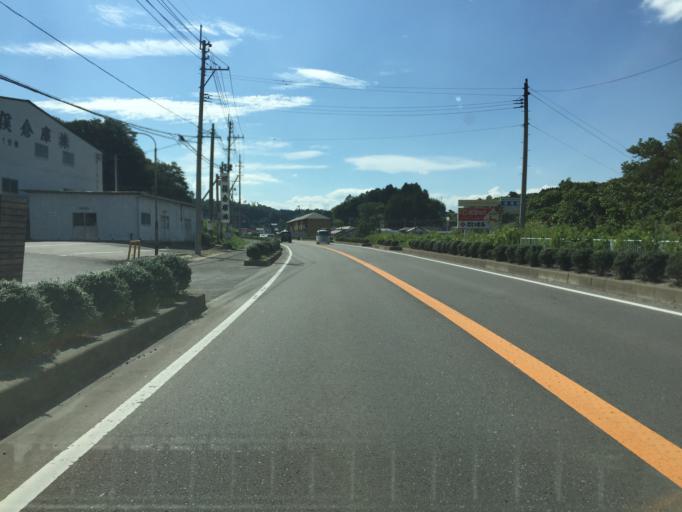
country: JP
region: Fukushima
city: Fukushima-shi
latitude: 37.6662
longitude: 140.5863
